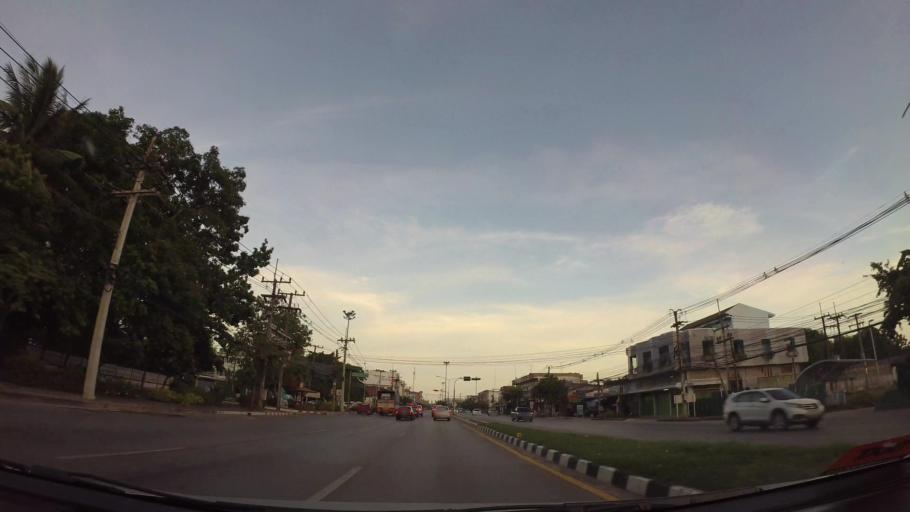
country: TH
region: Rayong
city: Rayong
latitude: 12.6755
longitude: 101.2891
